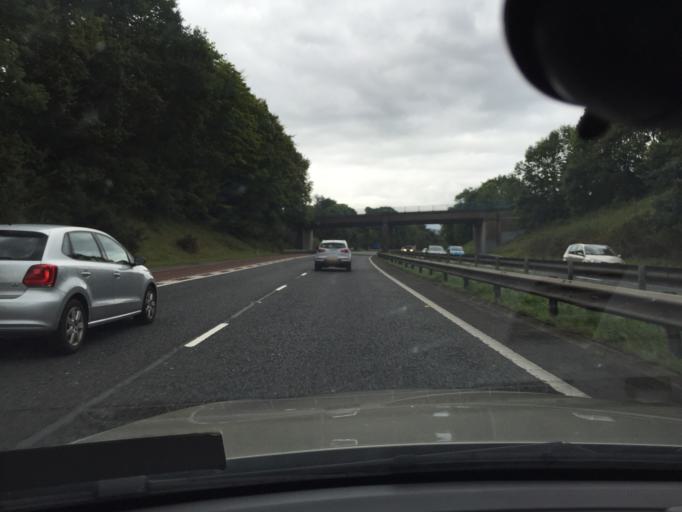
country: GB
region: Northern Ireland
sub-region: Lisburn District
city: Lisburn
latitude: 54.5499
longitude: -5.9963
